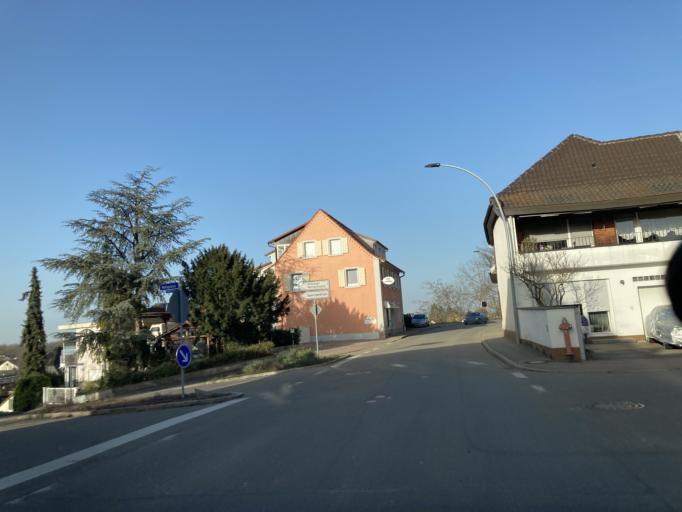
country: DE
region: Baden-Wuerttemberg
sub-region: Freiburg Region
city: Neuenburg am Rhein
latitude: 47.8163
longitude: 7.5608
